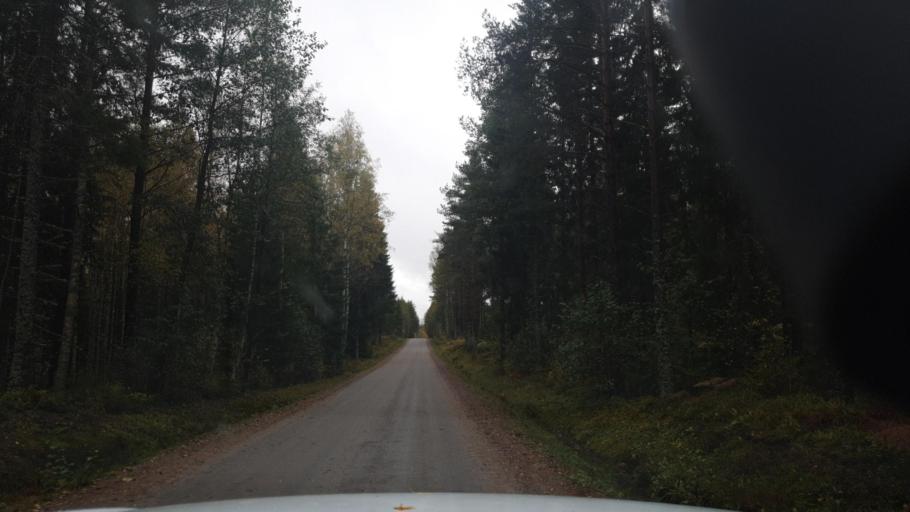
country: SE
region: Vaermland
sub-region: Karlstads Kommun
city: Edsvalla
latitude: 59.5283
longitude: 13.0004
